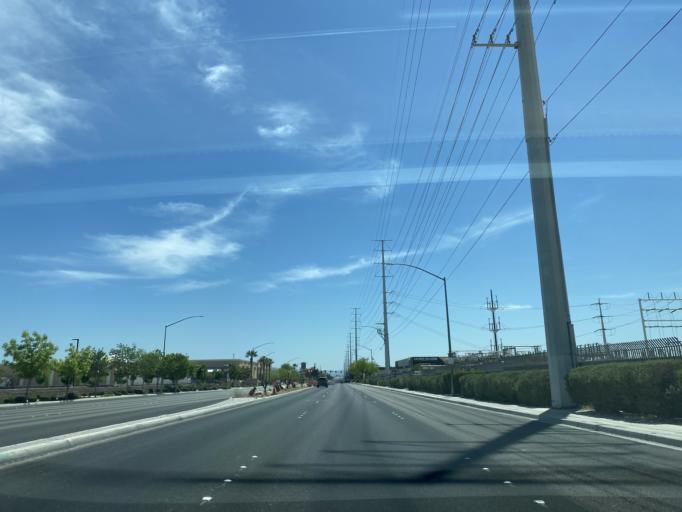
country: US
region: Nevada
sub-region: Clark County
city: North Las Vegas
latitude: 36.2449
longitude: -115.1169
